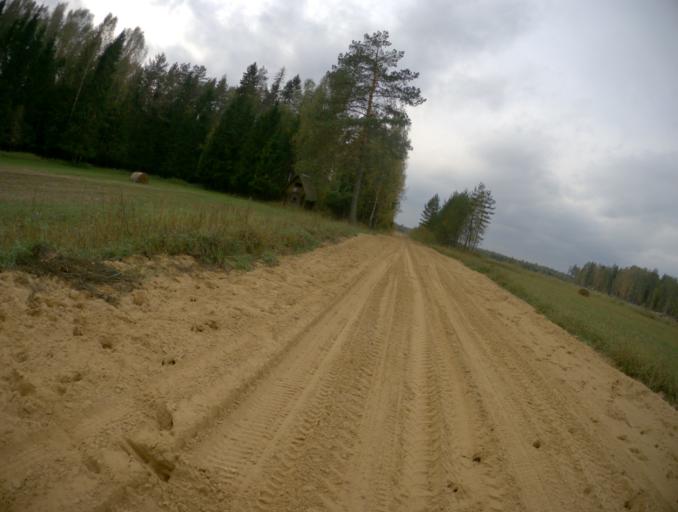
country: RU
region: Vladimir
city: Kideksha
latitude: 56.4710
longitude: 40.7160
